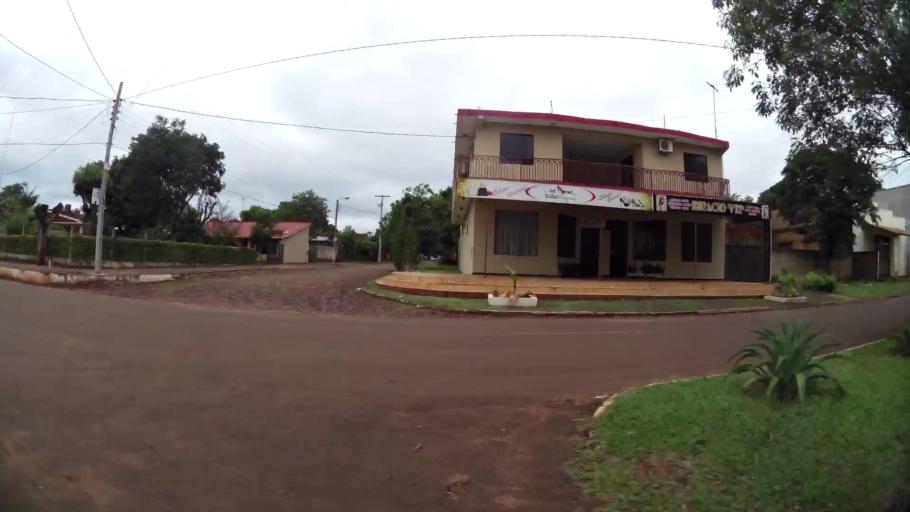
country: PY
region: Alto Parana
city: Presidente Franco
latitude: -25.4889
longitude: -54.7677
